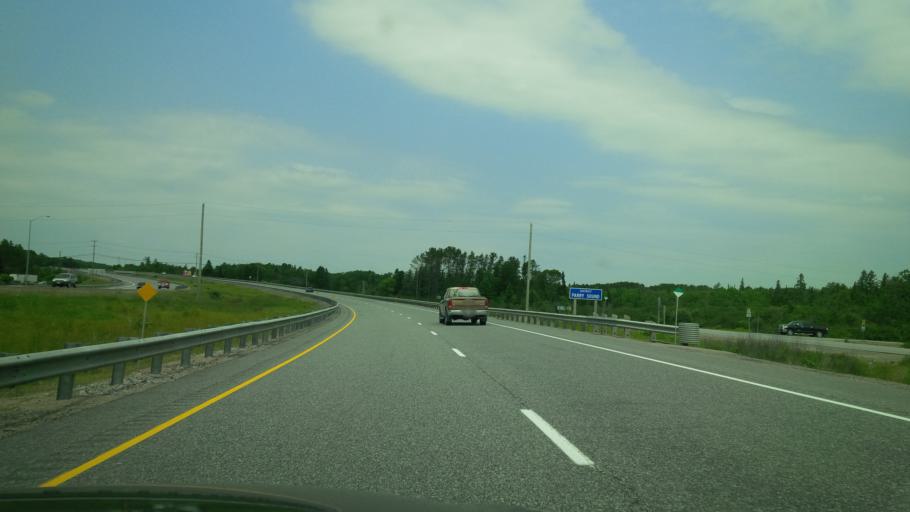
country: CA
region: Ontario
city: Huntsville
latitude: 45.4511
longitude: -79.2461
